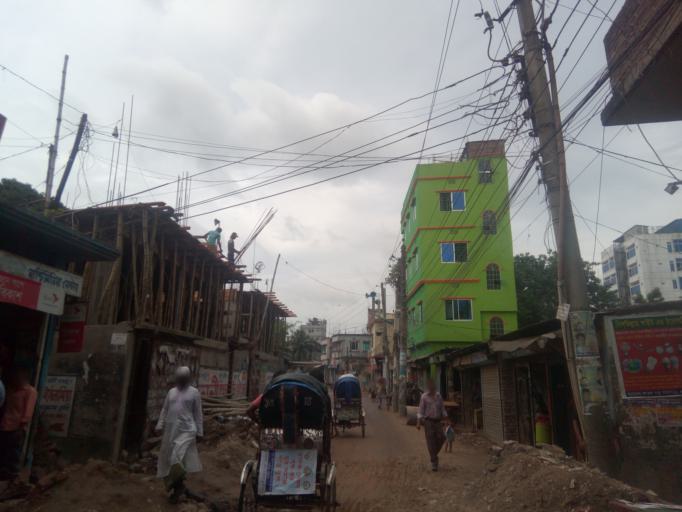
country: BD
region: Dhaka
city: Azimpur
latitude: 23.7091
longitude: 90.3734
